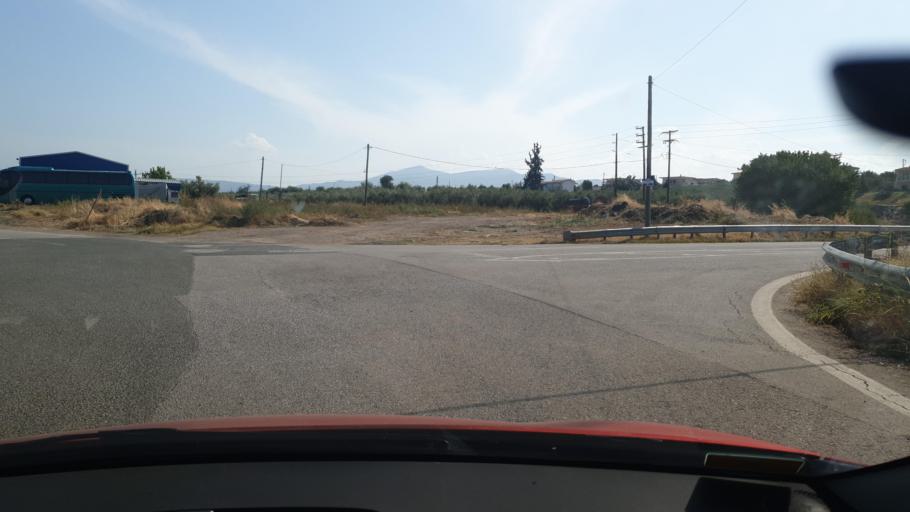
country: GR
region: Central Greece
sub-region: Nomos Fthiotidos
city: Livanates
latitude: 38.7067
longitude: 23.0546
